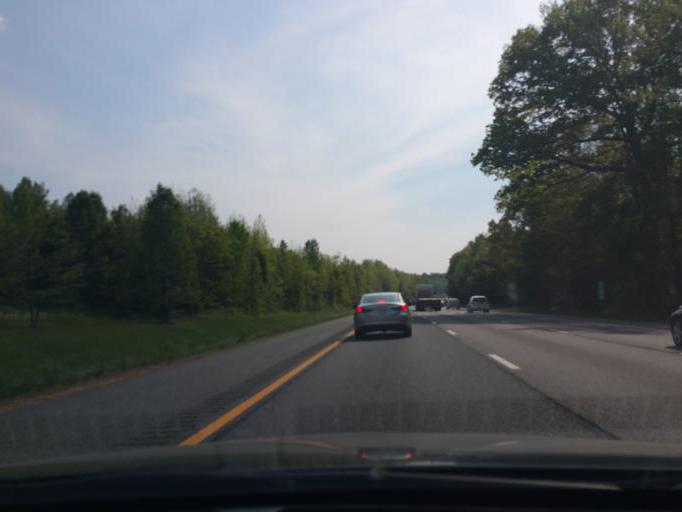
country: US
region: Maryland
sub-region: Harford County
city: Riverside
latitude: 39.4742
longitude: -76.2735
